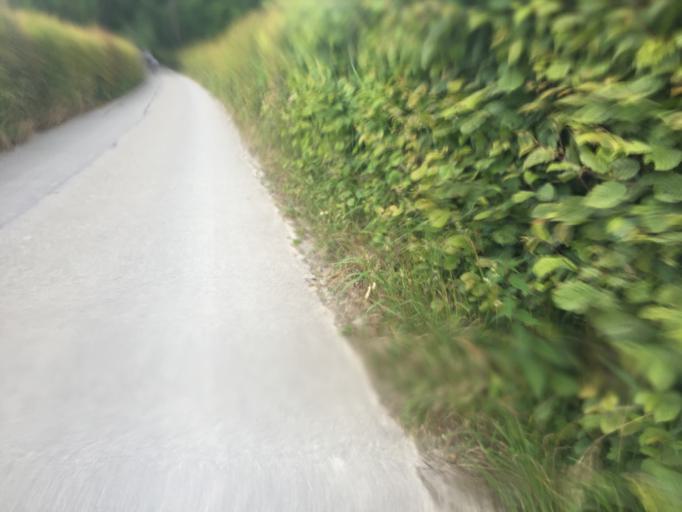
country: CH
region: Bern
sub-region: Bern-Mittelland District
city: Wohlen
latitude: 46.9643
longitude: 7.3589
